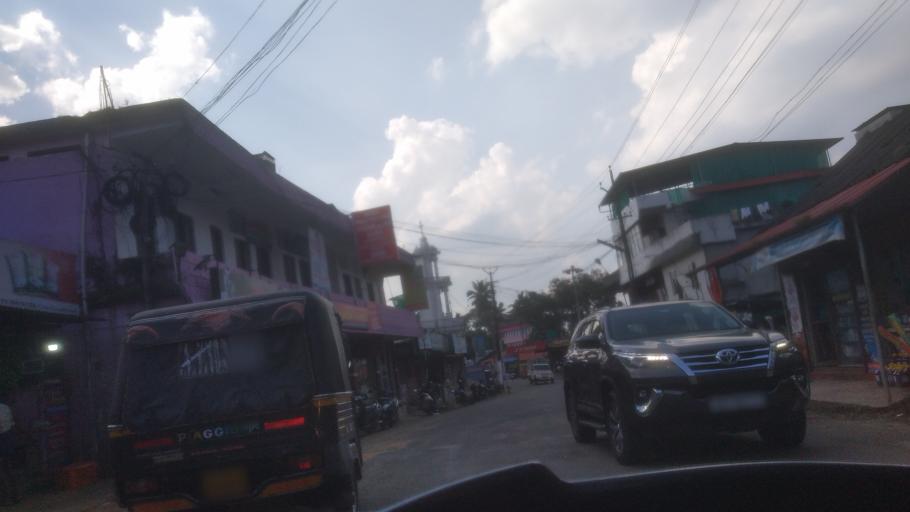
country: IN
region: Kerala
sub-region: Ernakulam
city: Kotamangalam
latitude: 10.0058
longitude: 76.6813
